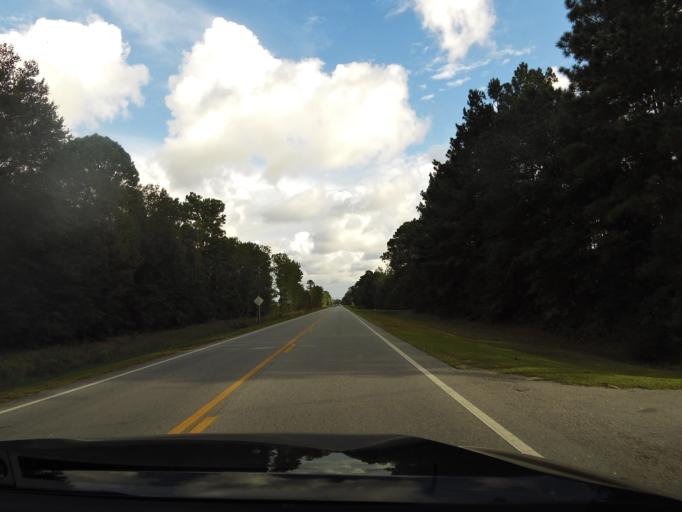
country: US
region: Georgia
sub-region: Liberty County
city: Midway
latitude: 31.7653
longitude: -81.4483
